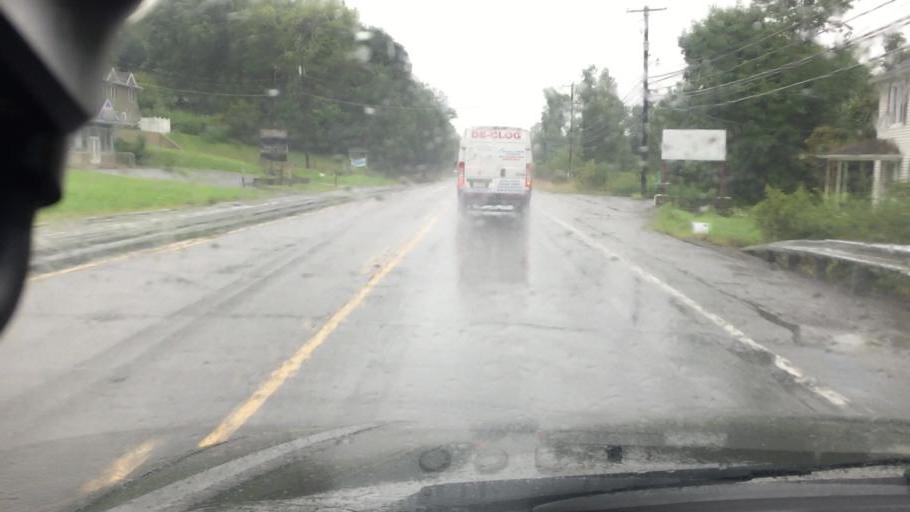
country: US
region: Pennsylvania
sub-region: Monroe County
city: Tannersville
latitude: 41.0235
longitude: -75.2982
